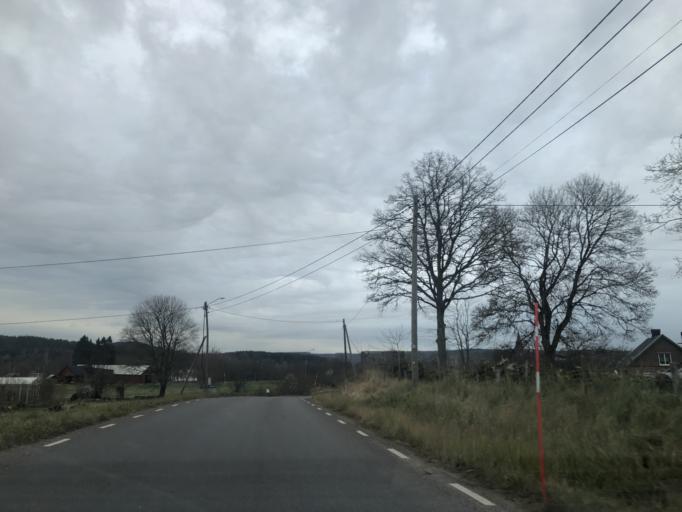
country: SE
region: Vaestra Goetaland
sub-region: Ulricehamns Kommun
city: Ulricehamn
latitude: 57.7979
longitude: 13.3600
